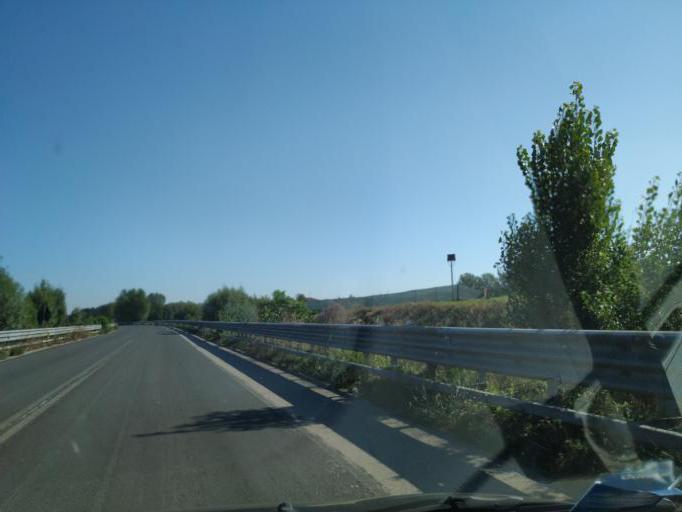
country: IT
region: Emilia-Romagna
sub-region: Provincia di Bologna
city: San Giovanni in Persiceto
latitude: 44.6462
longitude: 11.1725
